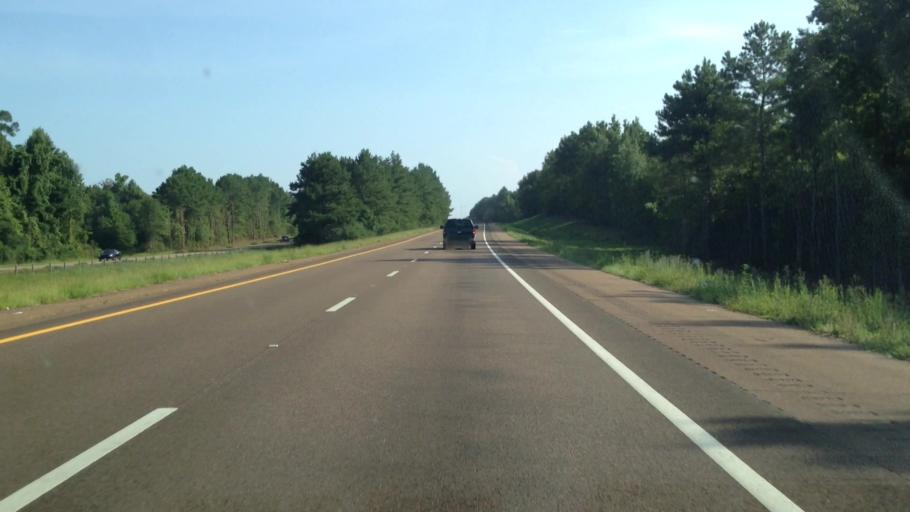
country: US
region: Mississippi
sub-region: Lincoln County
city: Brookhaven
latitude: 31.4433
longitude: -90.4796
